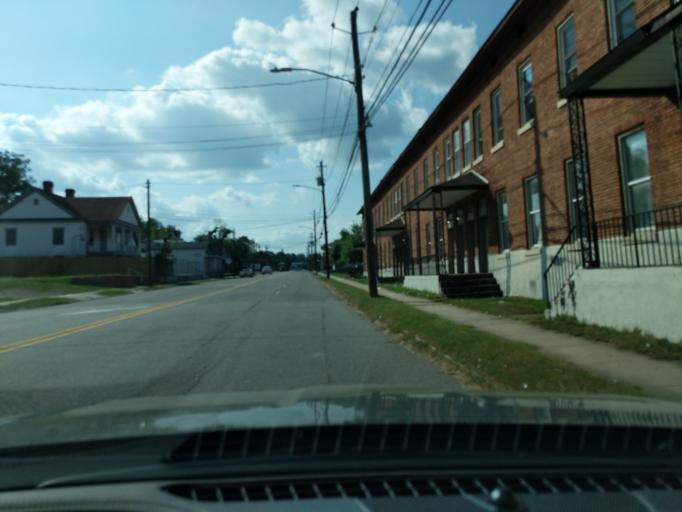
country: US
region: Georgia
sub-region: Richmond County
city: Augusta
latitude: 33.4858
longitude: -81.9971
